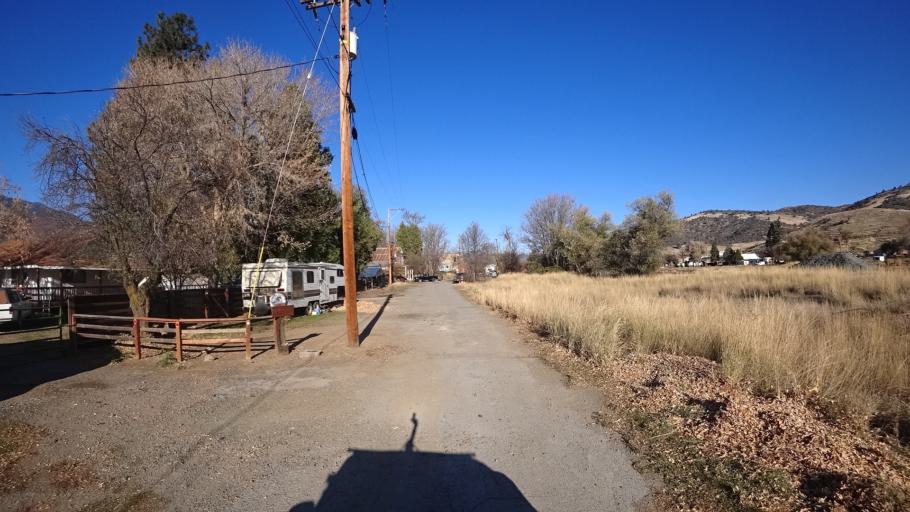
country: US
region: California
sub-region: Siskiyou County
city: Montague
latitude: 41.9089
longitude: -122.5548
